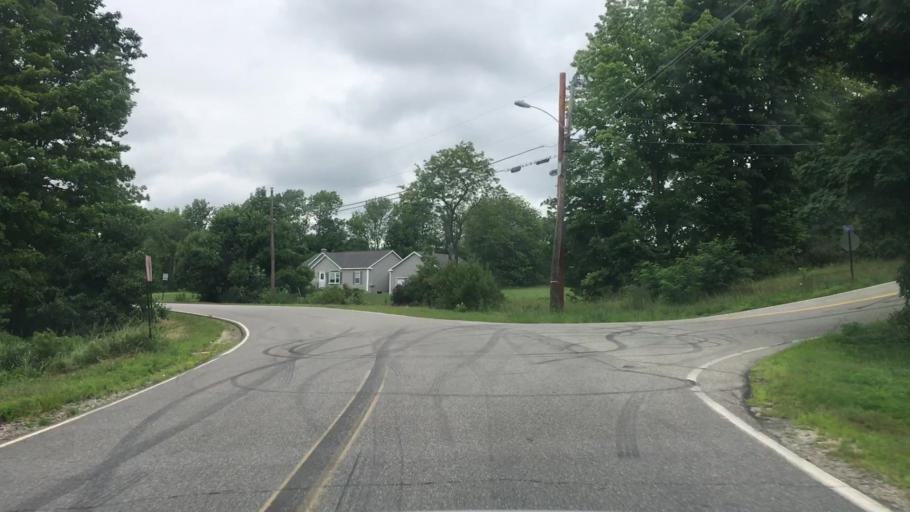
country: US
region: Maine
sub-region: York County
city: Biddeford
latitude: 43.5196
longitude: -70.5138
